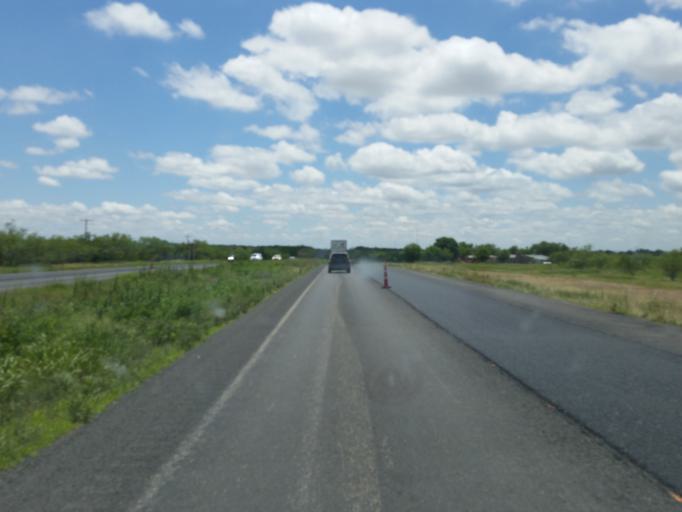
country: US
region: Texas
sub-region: Scurry County
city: Snyder
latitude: 32.7664
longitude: -100.9356
